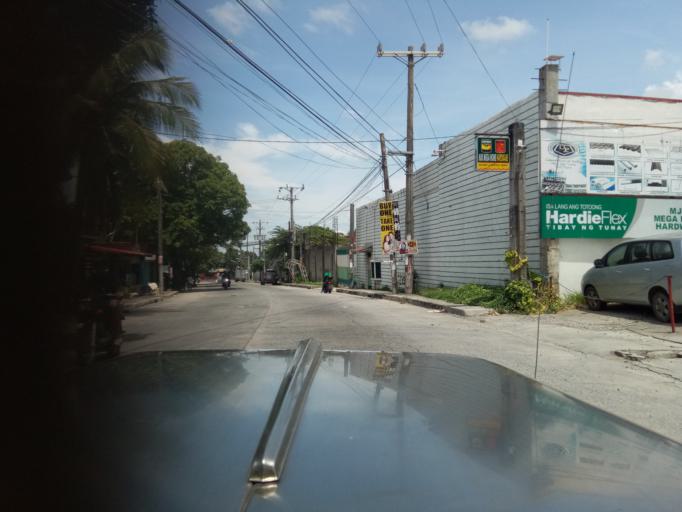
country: PH
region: Calabarzon
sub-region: Province of Cavite
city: Bulihan
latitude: 14.2874
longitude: 120.9979
